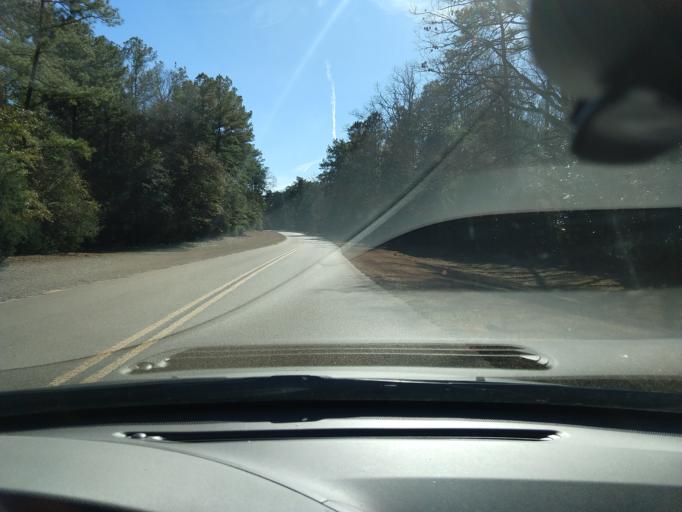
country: US
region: Georgia
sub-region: Macon County
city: Oglethorpe
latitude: 32.2057
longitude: -84.1284
